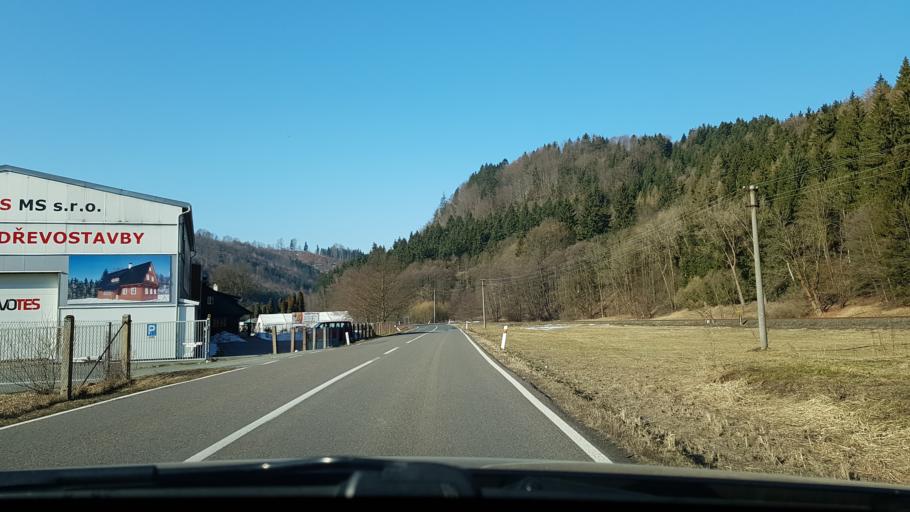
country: CZ
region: Olomoucky
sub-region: Okres Sumperk
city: Hanusovice
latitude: 50.0788
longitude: 16.9616
